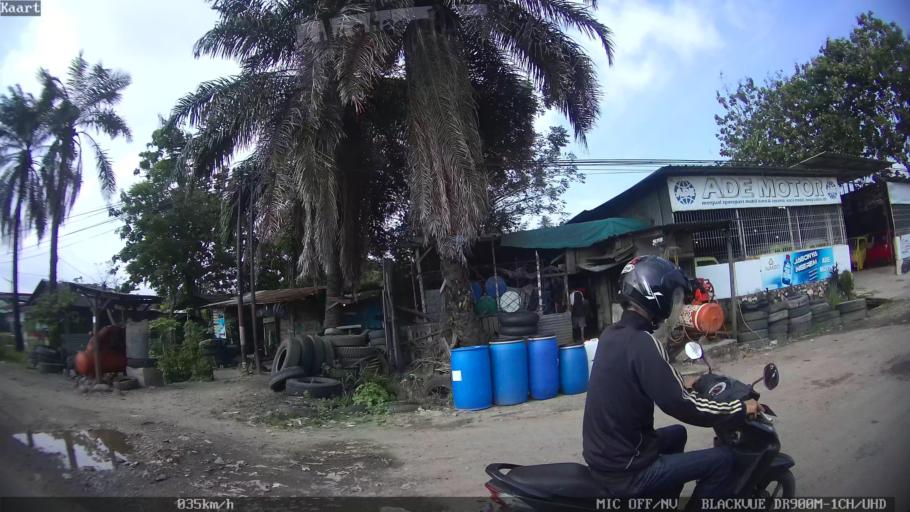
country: ID
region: Lampung
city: Kedaton
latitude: -5.3659
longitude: 105.2653
